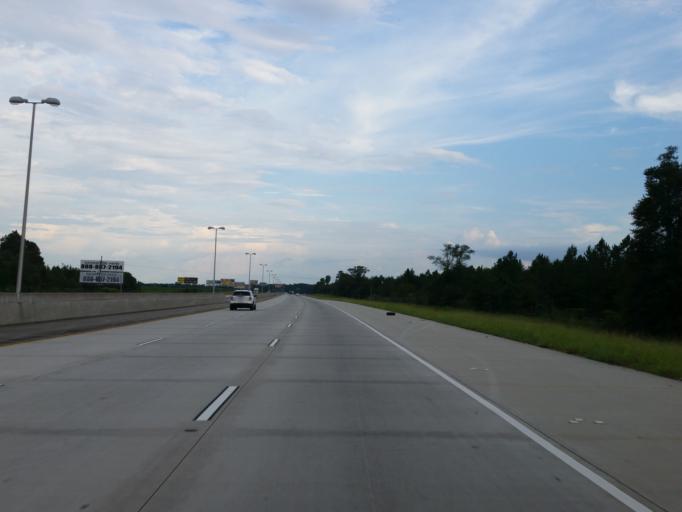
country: US
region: Georgia
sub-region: Cook County
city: Adel
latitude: 31.0706
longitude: -83.4059
